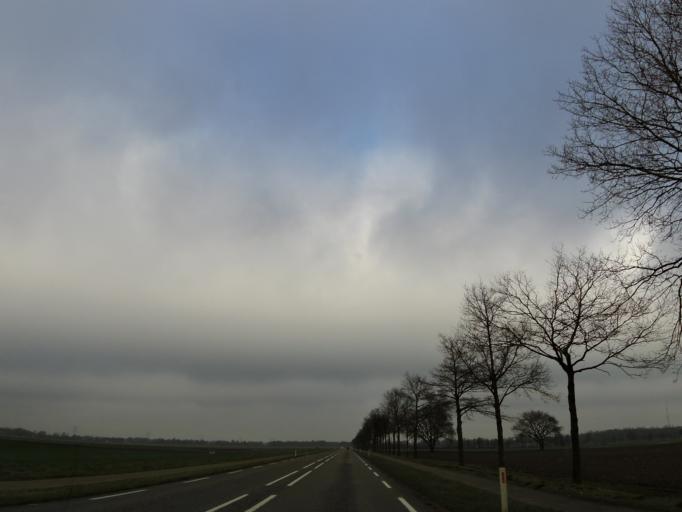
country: NL
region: Limburg
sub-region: Gemeente Peel en Maas
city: Maasbree
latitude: 51.4122
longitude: 5.9613
